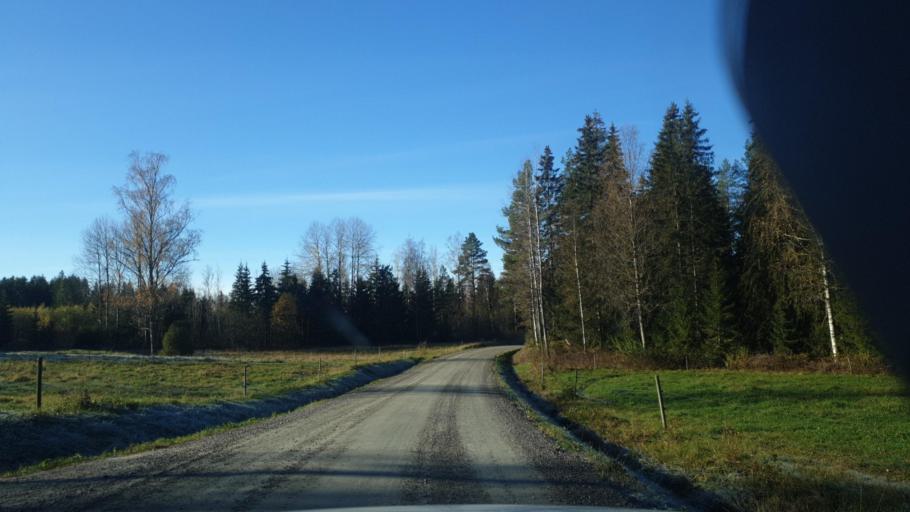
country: SE
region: Vaermland
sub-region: Karlstads Kommun
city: Edsvalla
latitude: 59.5571
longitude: 13.0256
